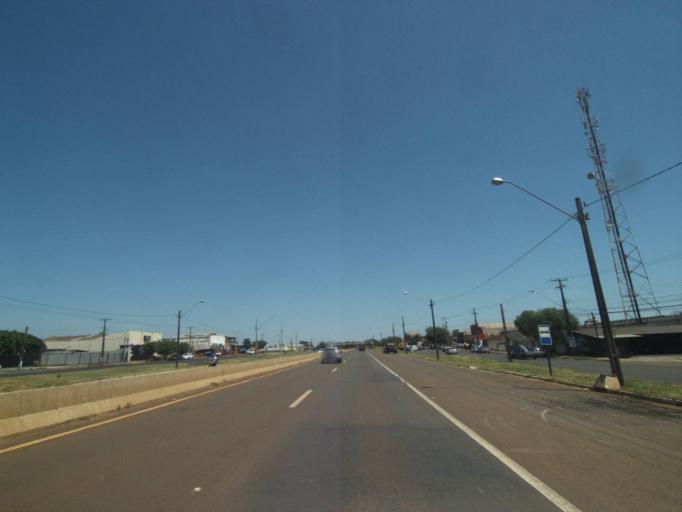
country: BR
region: Parana
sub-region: Londrina
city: Londrina
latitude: -23.3668
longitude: -51.1428
